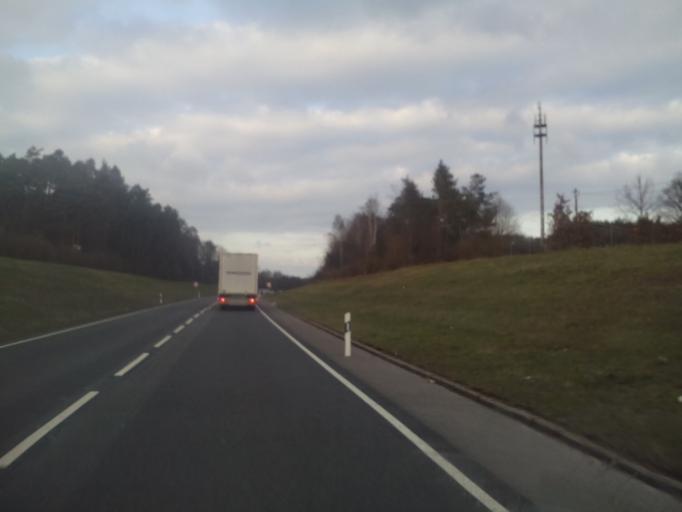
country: DE
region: Bavaria
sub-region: Upper Franconia
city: Frensdorf
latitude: 49.7646
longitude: 10.8754
